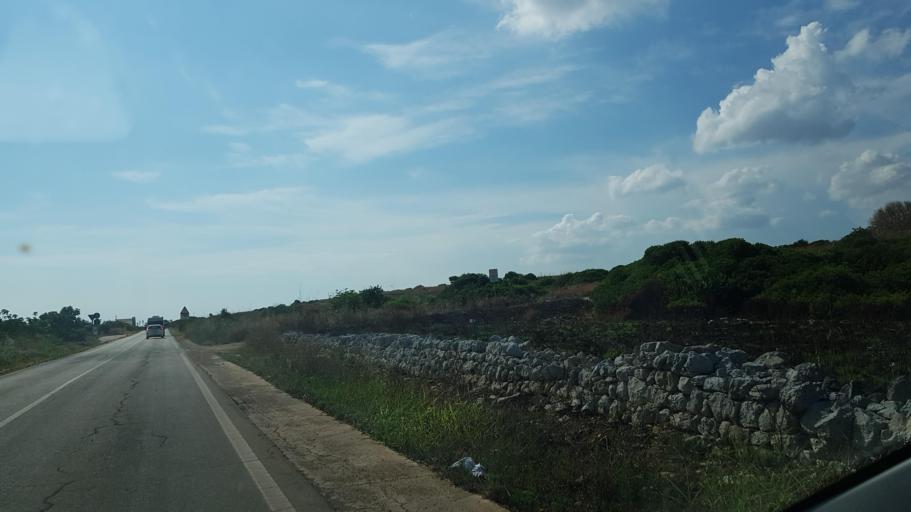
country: IT
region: Apulia
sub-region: Provincia di Lecce
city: Salve
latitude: 39.8382
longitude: 18.2354
